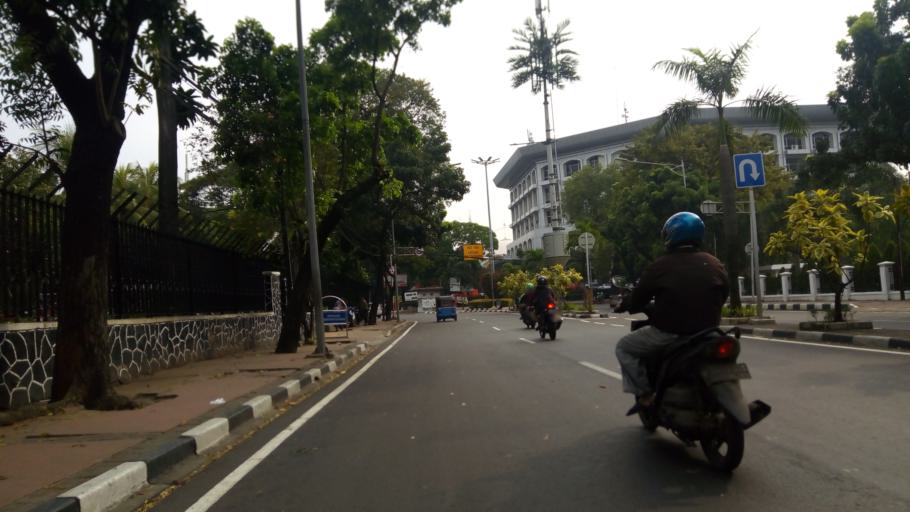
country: ID
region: Jakarta Raya
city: Jakarta
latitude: -6.1677
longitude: 106.8367
